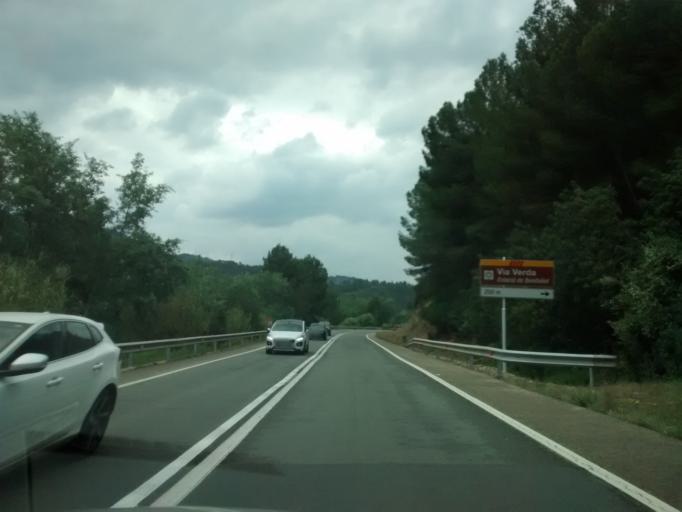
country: ES
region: Catalonia
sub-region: Provincia de Tarragona
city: Benifallet
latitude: 40.9665
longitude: 0.5096
